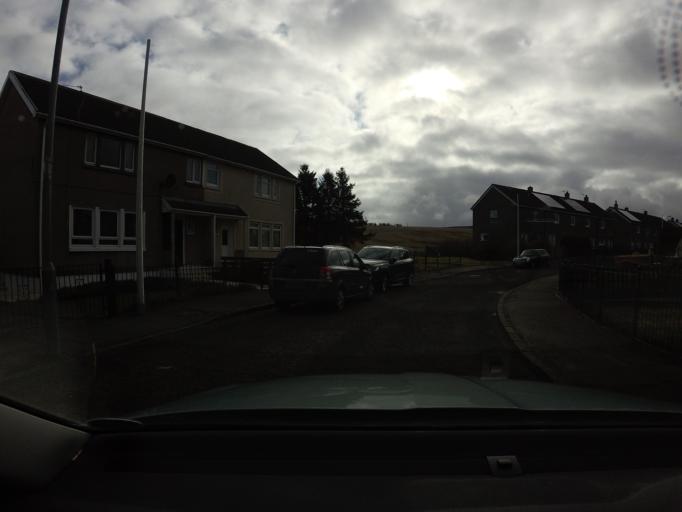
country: GB
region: Scotland
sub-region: South Lanarkshire
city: Lanark
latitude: 55.5977
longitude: -3.7764
